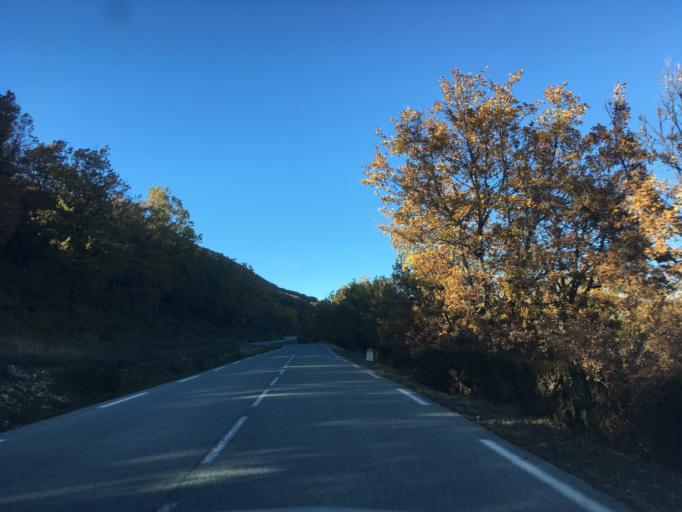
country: FR
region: Provence-Alpes-Cote d'Azur
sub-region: Departement du Var
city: Bargemon
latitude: 43.6840
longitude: 6.5109
